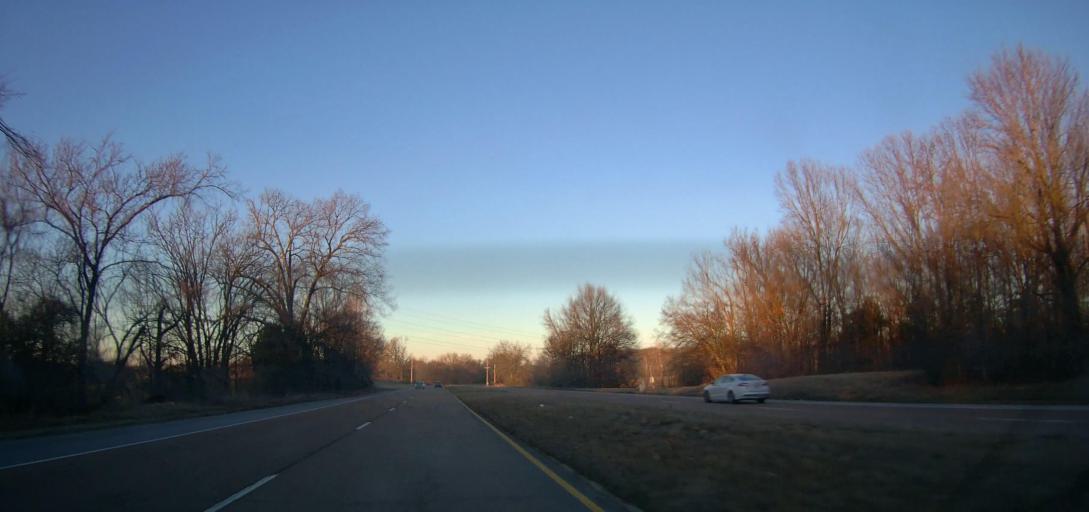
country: US
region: Tennessee
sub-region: Shelby County
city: Bartlett
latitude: 35.2507
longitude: -89.8952
